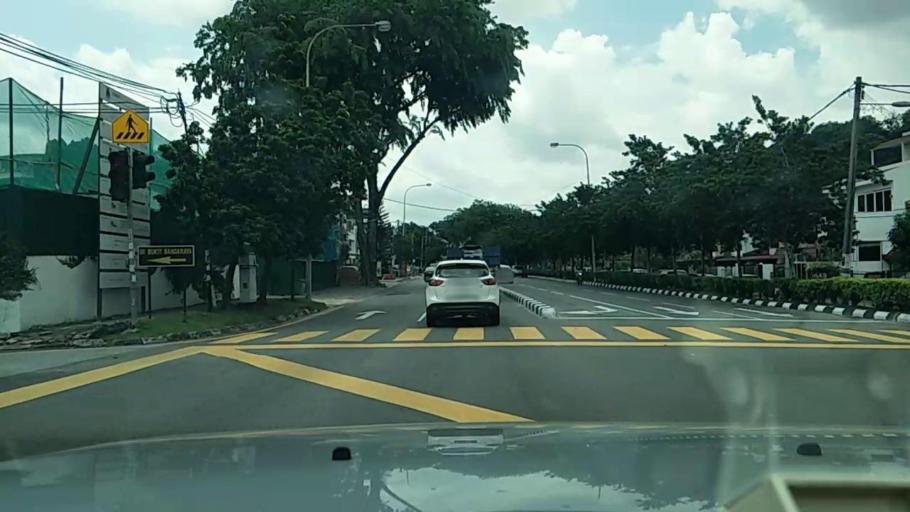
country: MY
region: Kuala Lumpur
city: Kuala Lumpur
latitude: 3.1381
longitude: 101.6726
